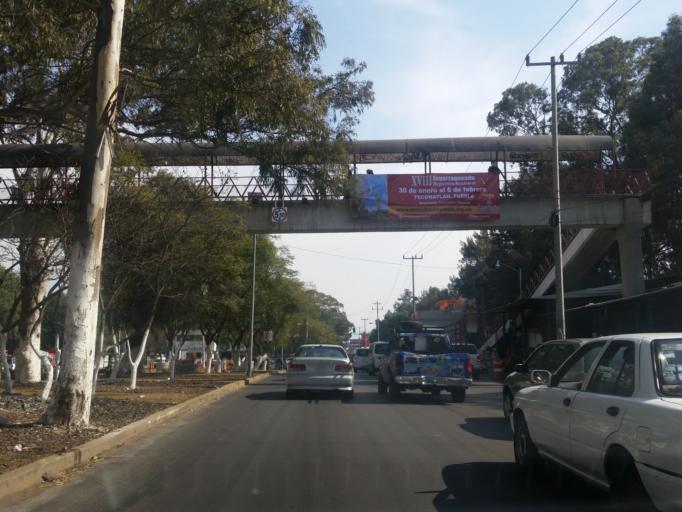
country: MX
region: Mexico
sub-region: La Paz
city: San Isidro
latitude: 19.3218
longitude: -98.9419
